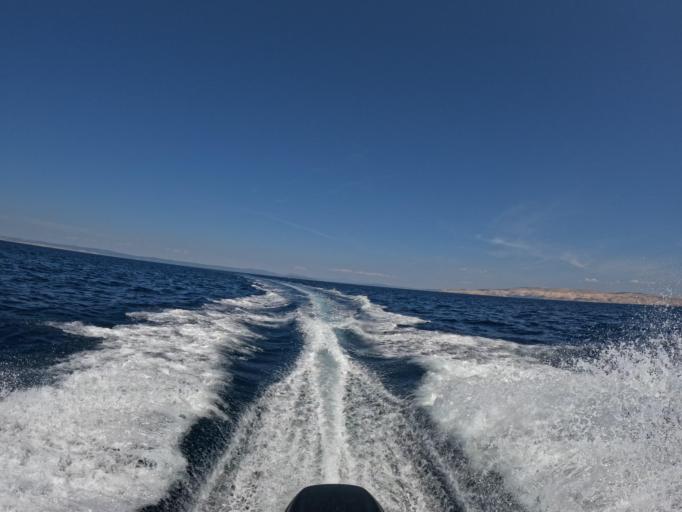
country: HR
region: Primorsko-Goranska
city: Lopar
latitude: 44.8594
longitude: 14.6936
